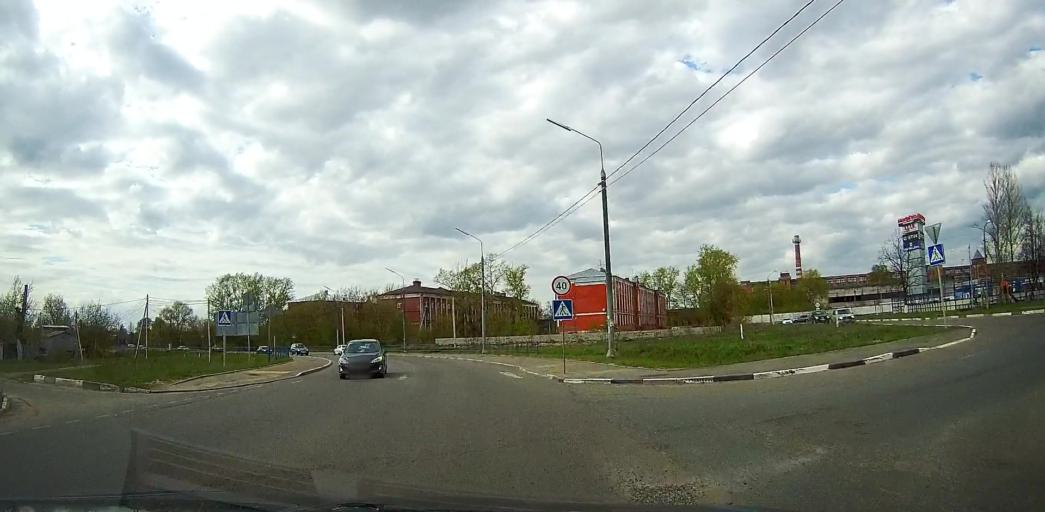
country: RU
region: Moskovskaya
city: Pavlovskiy Posad
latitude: 55.7695
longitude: 38.6496
